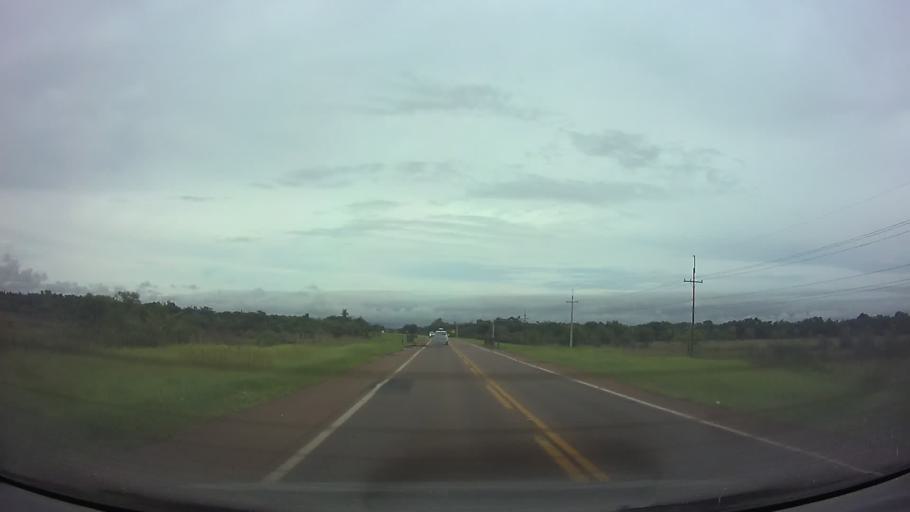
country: PY
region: Paraguari
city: Carapegua
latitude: -25.7296
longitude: -57.2065
